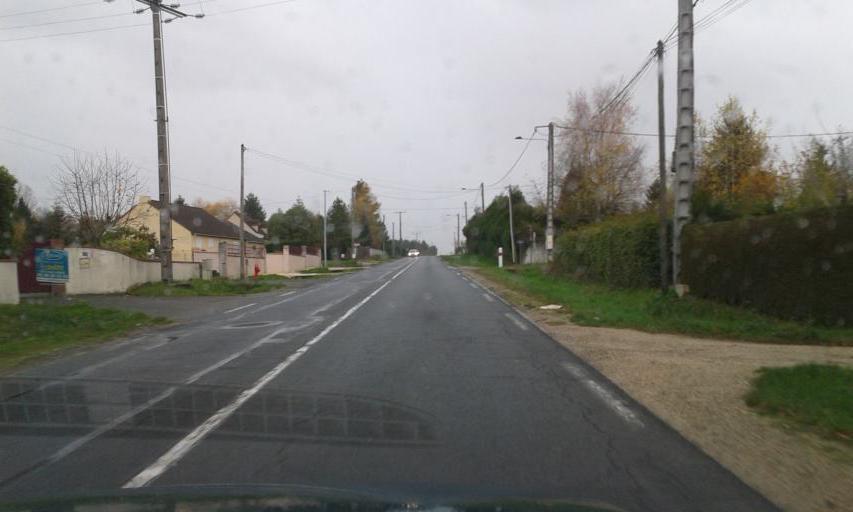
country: FR
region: Centre
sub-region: Departement du Loiret
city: Fay-aux-Loges
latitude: 47.9193
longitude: 2.1358
